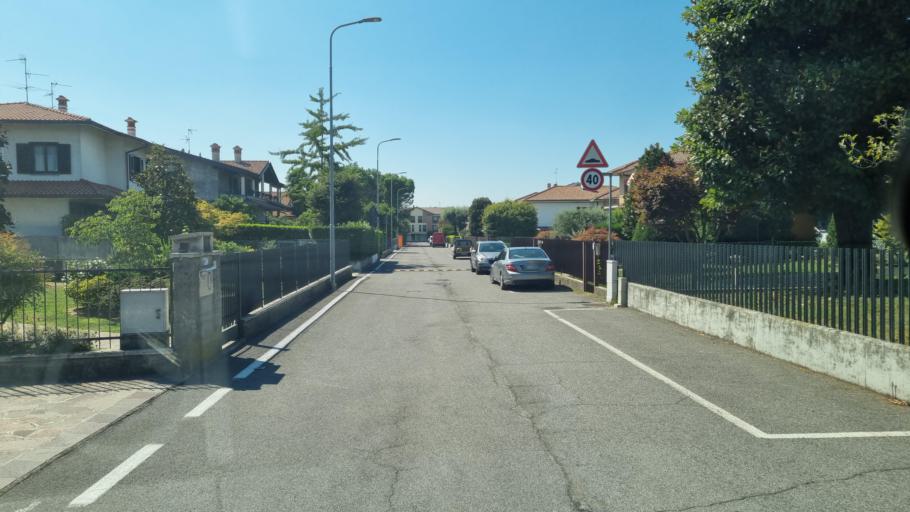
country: IT
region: Lombardy
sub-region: Provincia di Bergamo
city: Azzano San Paolo
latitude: 45.6560
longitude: 9.6669
